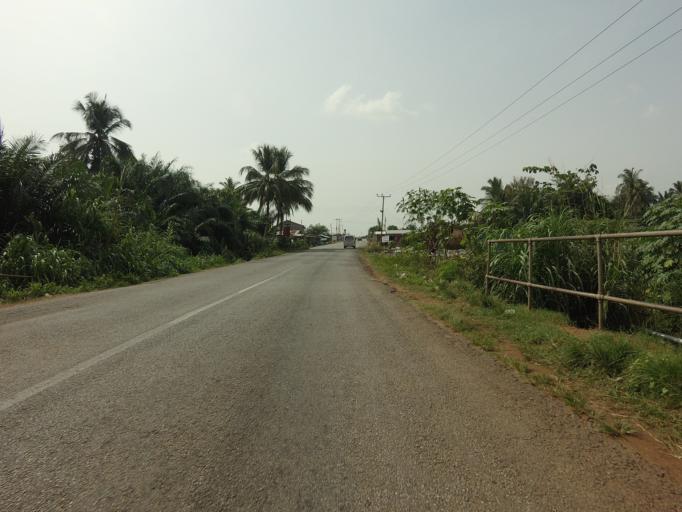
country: GH
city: Akropong
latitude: 6.2597
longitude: 0.1353
